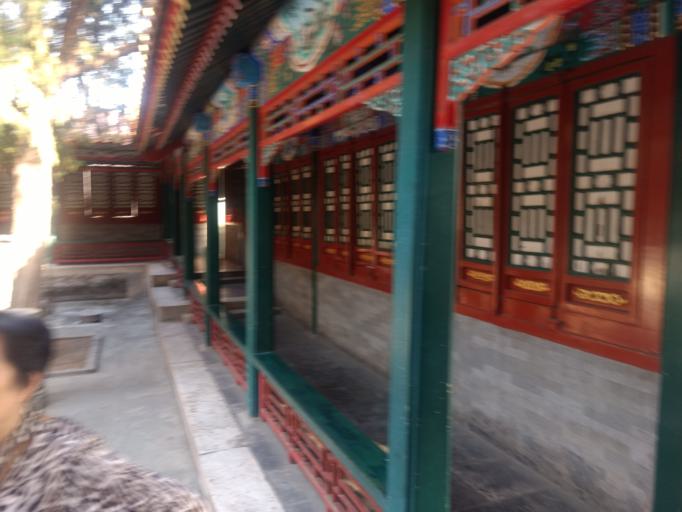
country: CN
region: Beijing
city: Haidian
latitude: 39.9969
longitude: 116.2682
